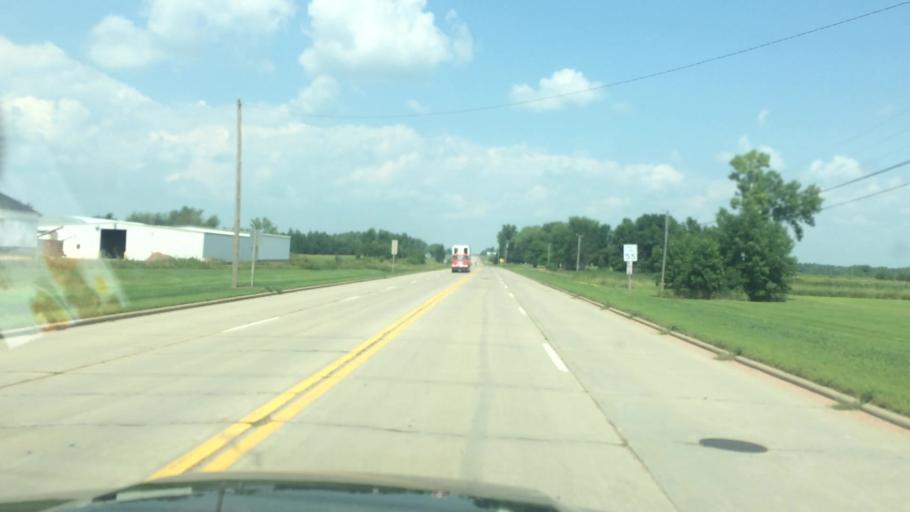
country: US
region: Wisconsin
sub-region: Clark County
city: Colby
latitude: 44.8526
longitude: -90.3160
